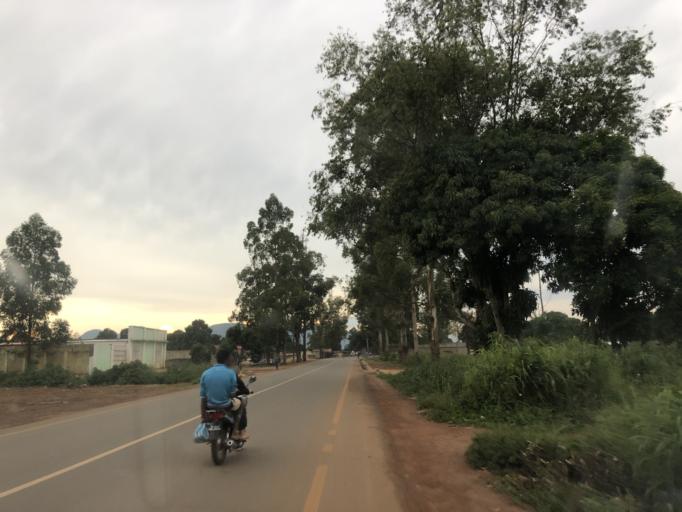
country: AO
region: Cuanza Sul
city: Uacu Cungo
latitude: -11.3519
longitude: 15.1159
